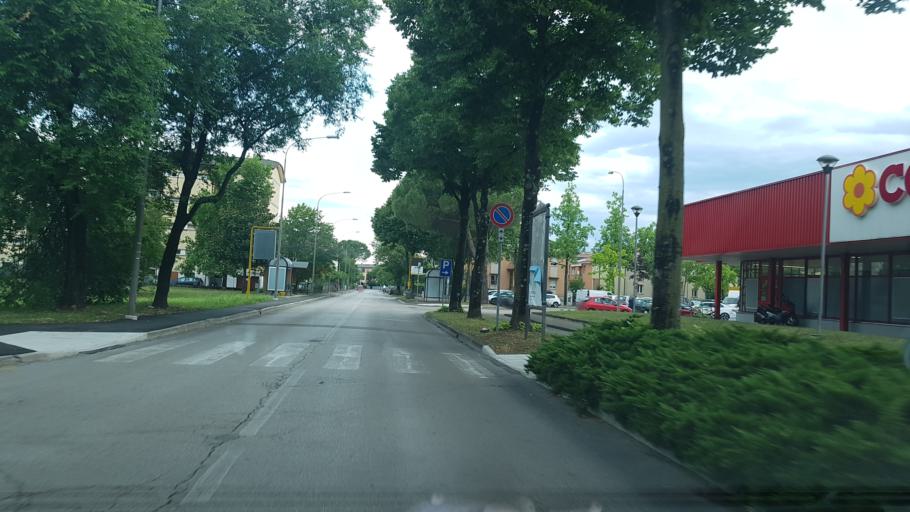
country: IT
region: Friuli Venezia Giulia
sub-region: Provincia di Gorizia
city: Gorizia
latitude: 45.9296
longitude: 13.6182
